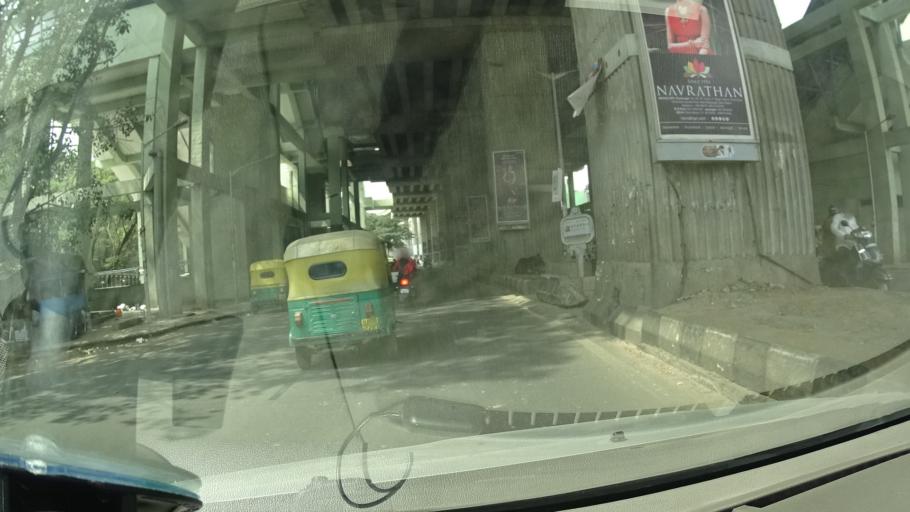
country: IN
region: Karnataka
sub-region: Bangalore Urban
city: Bangalore
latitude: 12.9983
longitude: 77.5576
